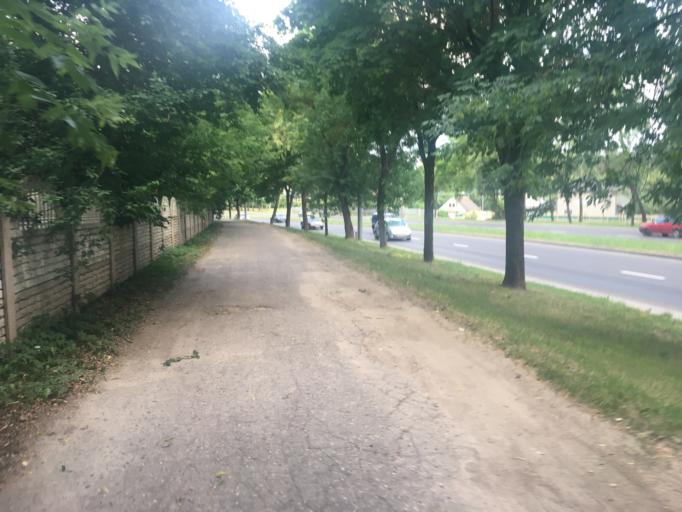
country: BY
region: Grodnenskaya
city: Hrodna
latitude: 53.6857
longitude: 23.8016
